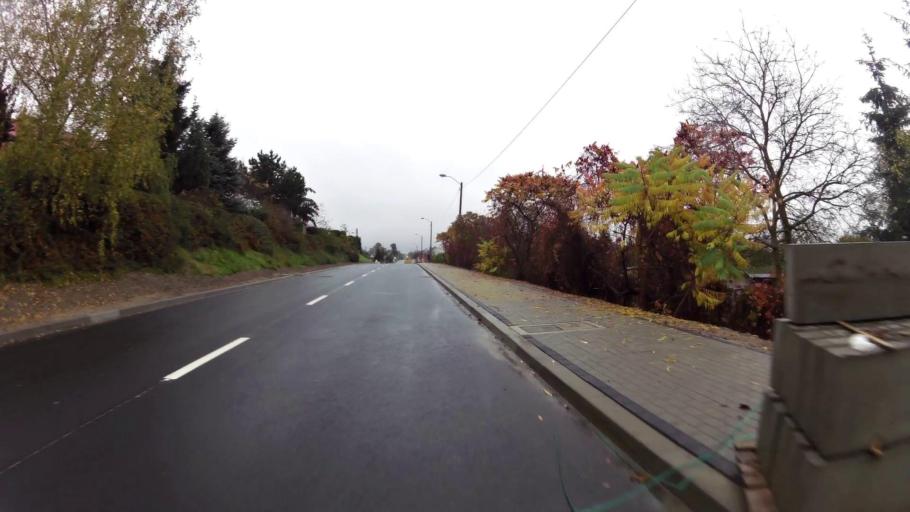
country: PL
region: West Pomeranian Voivodeship
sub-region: Powiat gryfinski
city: Gryfino
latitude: 53.2462
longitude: 14.4989
